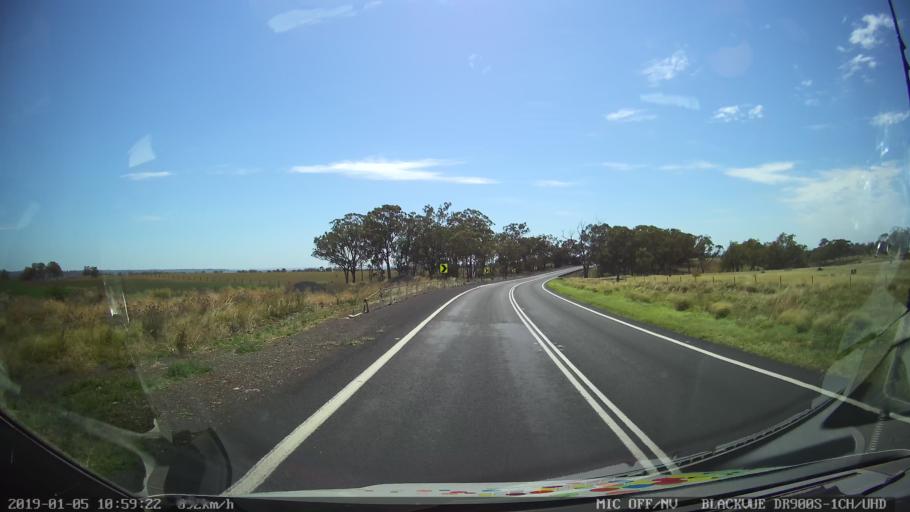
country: AU
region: New South Wales
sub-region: Warrumbungle Shire
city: Coonabarabran
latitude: -31.4155
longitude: 149.1948
